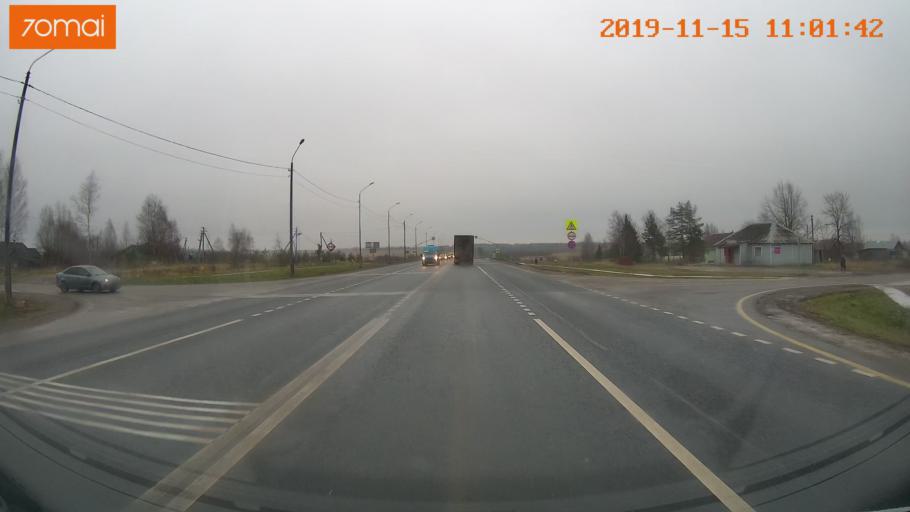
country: RU
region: Vologda
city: Chebsara
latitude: 59.1318
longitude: 38.9259
